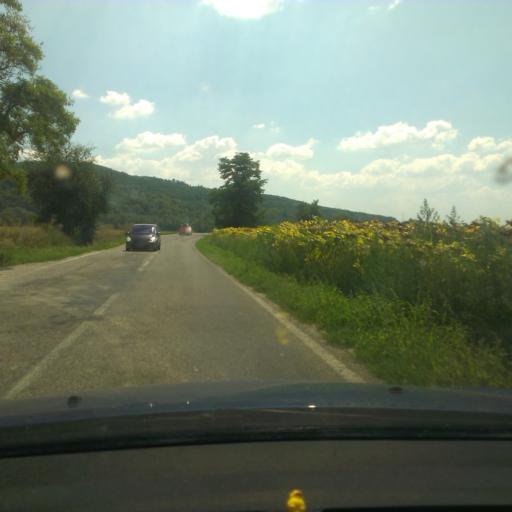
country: SK
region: Trnavsky
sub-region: Okres Trnava
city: Piestany
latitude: 48.5280
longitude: 17.8321
